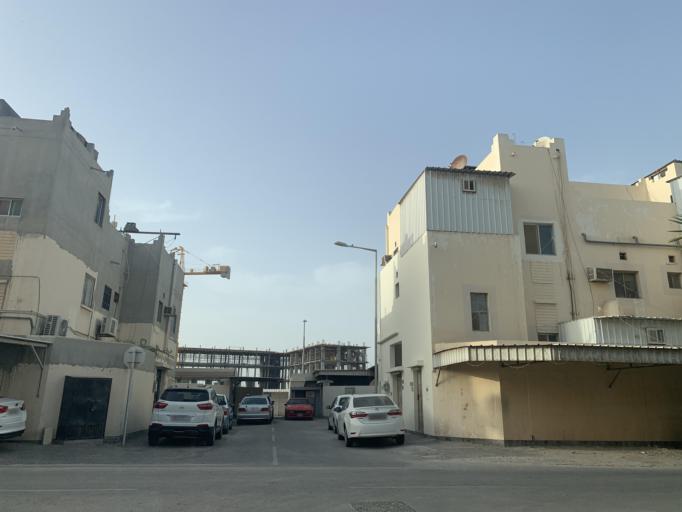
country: BH
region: Northern
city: Madinat `Isa
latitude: 26.1637
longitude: 50.5098
